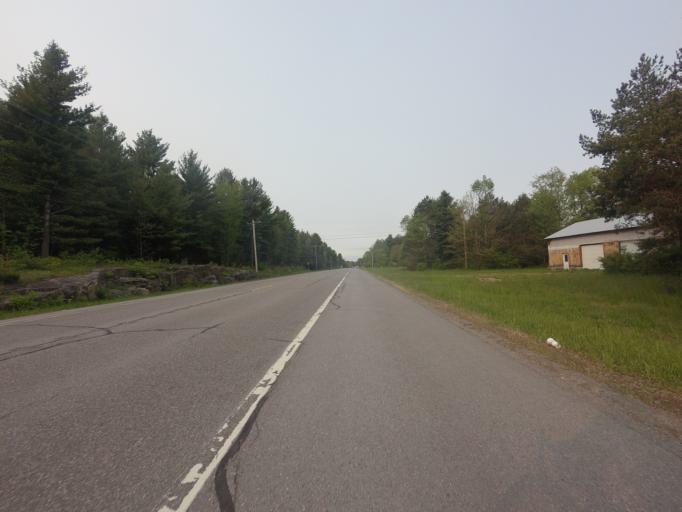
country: US
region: New York
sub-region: Jefferson County
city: Carthage
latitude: 44.0874
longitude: -75.4292
